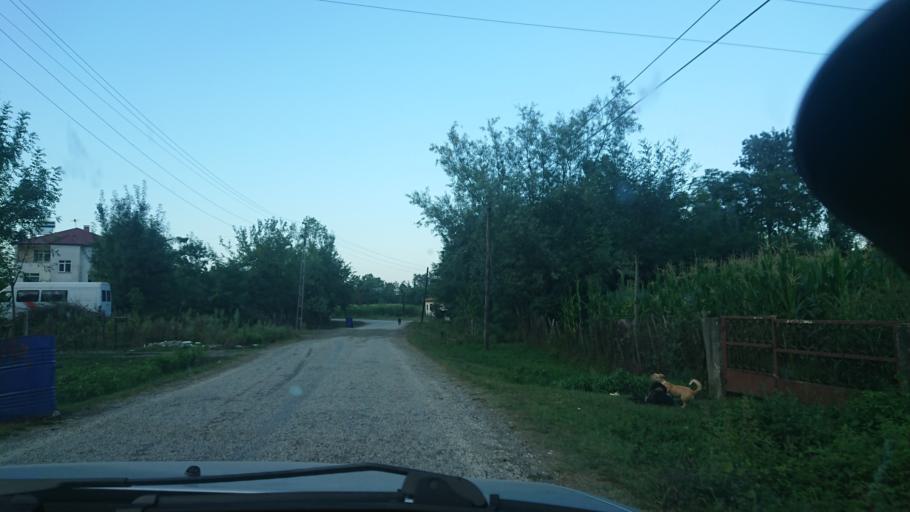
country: TR
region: Samsun
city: Dikbiyik
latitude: 41.1781
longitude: 36.5461
